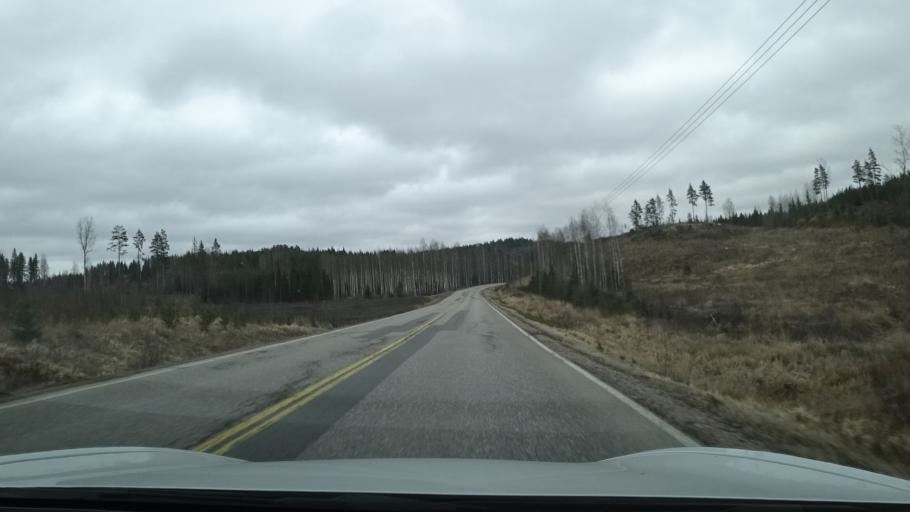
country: FI
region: Uusimaa
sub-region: Porvoo
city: Myrskylae
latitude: 60.6674
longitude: 25.7793
